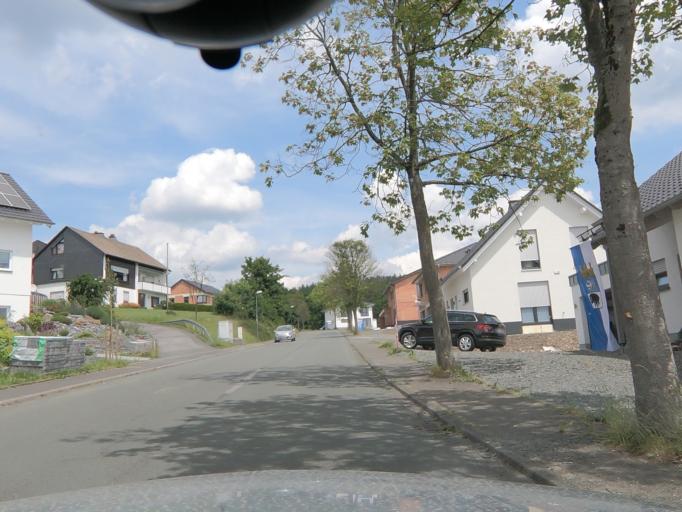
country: DE
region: North Rhine-Westphalia
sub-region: Regierungsbezirk Arnsberg
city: Meschede
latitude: 51.3721
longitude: 8.3379
